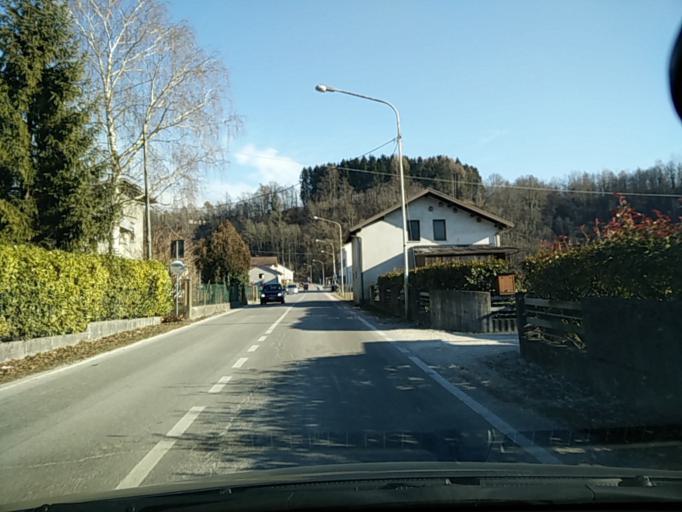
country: IT
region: Veneto
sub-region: Provincia di Belluno
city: Pieve d'Alpago
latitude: 46.1506
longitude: 12.3282
